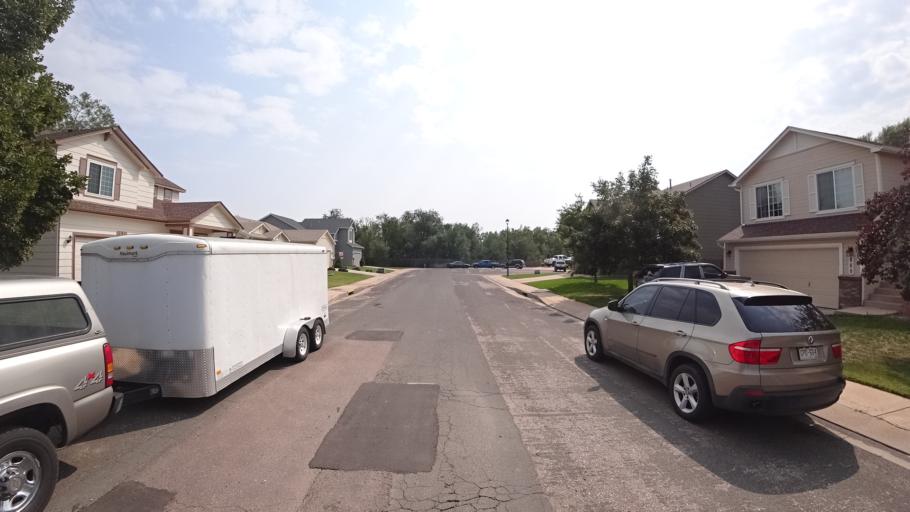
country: US
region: Colorado
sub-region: El Paso County
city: Cimarron Hills
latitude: 38.8209
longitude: -104.7394
